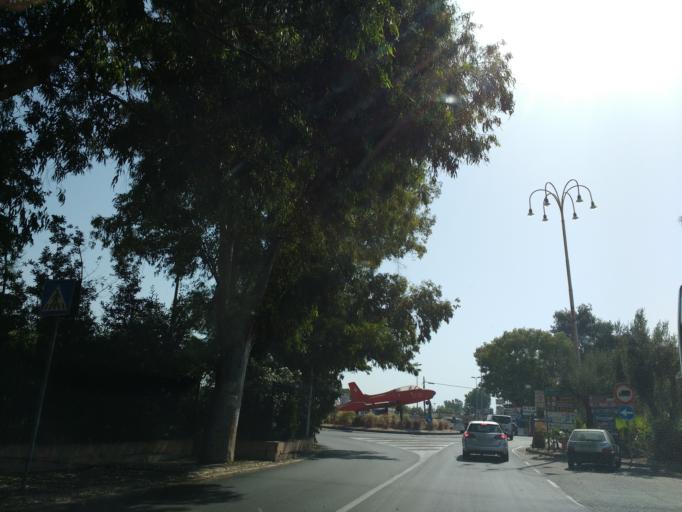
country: IT
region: Sicily
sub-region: Catania
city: Catania
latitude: 37.4741
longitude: 15.0746
